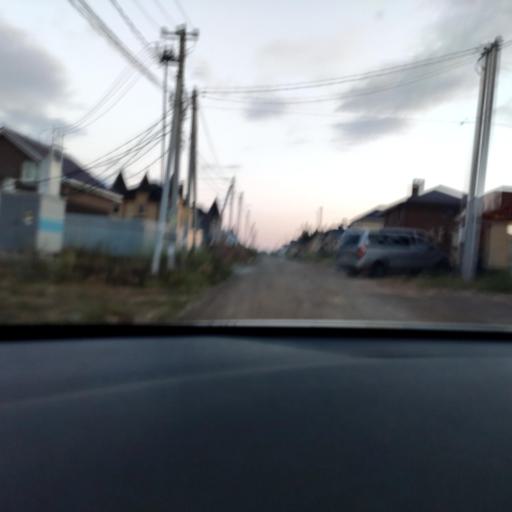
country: RU
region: Tatarstan
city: Stolbishchi
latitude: 55.7222
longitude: 49.3001
